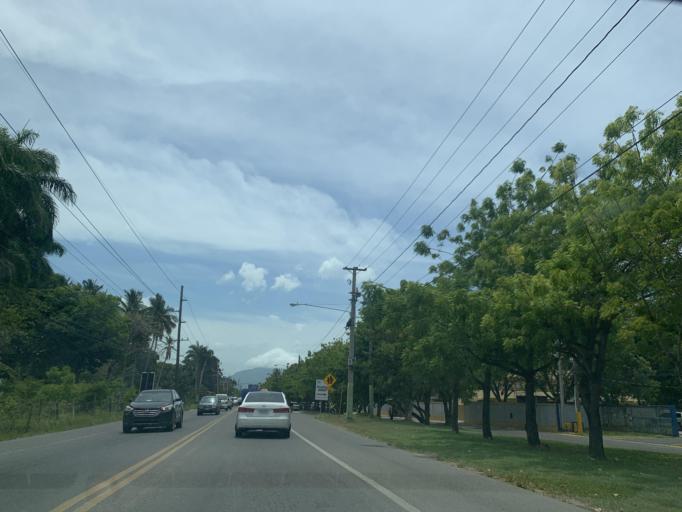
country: DO
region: Puerto Plata
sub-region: Puerto Plata
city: Puerto Plata
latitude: 19.7502
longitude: -70.5726
